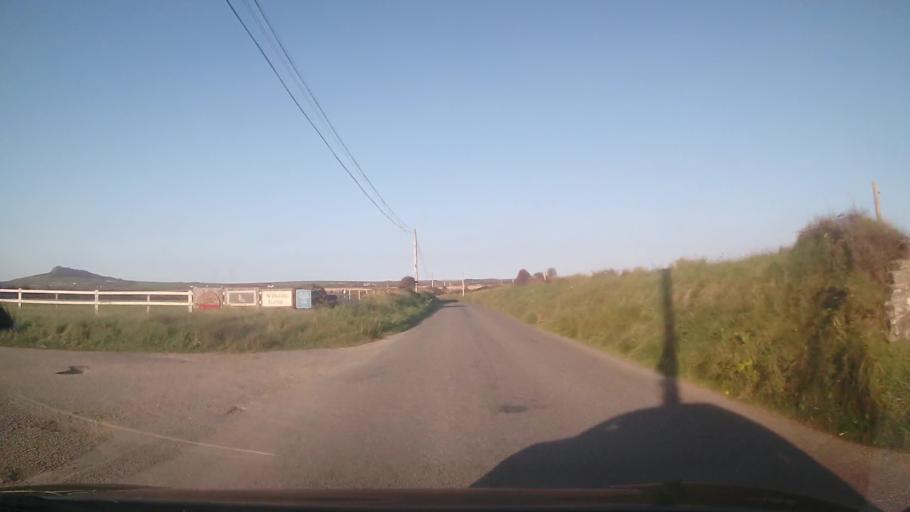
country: GB
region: Wales
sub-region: Pembrokeshire
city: Saint David's
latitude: 51.8895
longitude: -5.2569
